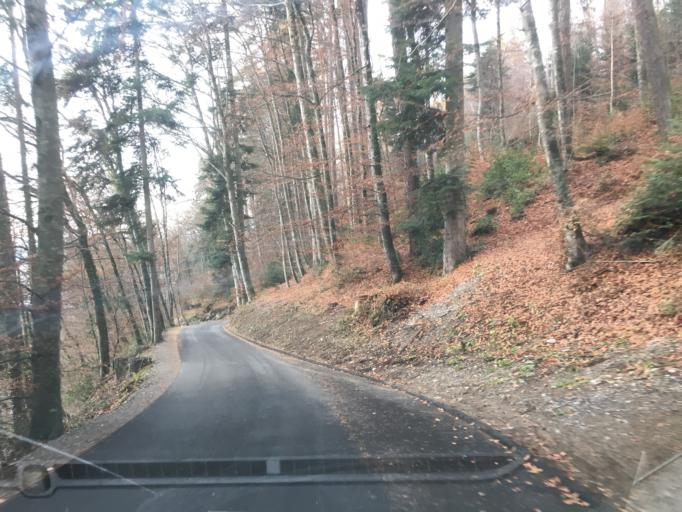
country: AT
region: Vorarlberg
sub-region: Politischer Bezirk Feldkirch
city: Klaus
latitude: 47.3152
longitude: 9.6588
